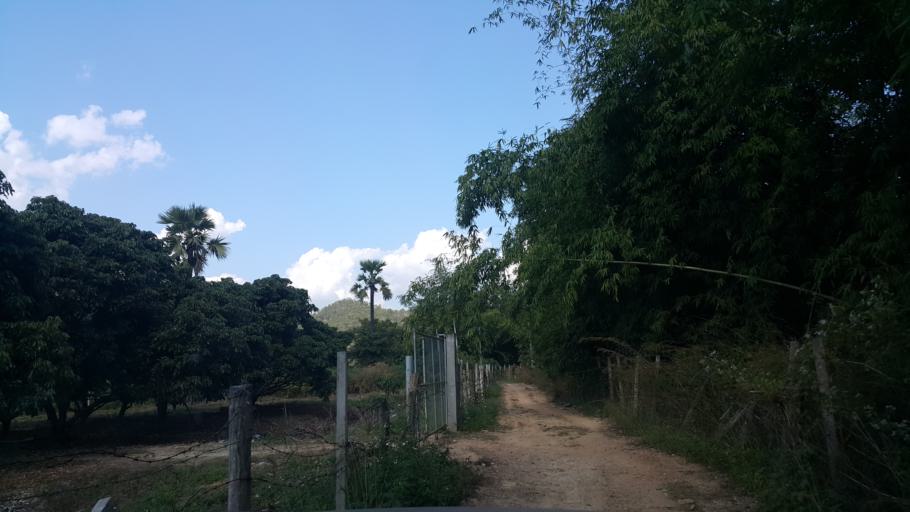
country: TH
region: Lamphun
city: Ban Thi
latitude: 18.5915
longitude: 99.1622
